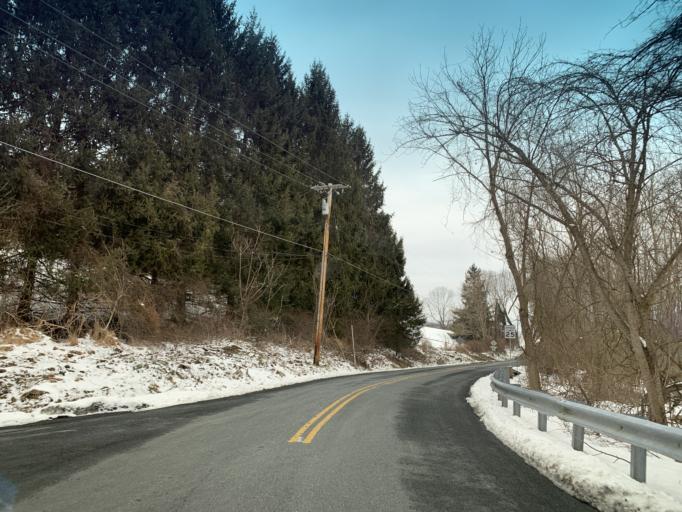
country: US
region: Maryland
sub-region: Harford County
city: Jarrettsville
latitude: 39.5842
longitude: -76.4931
